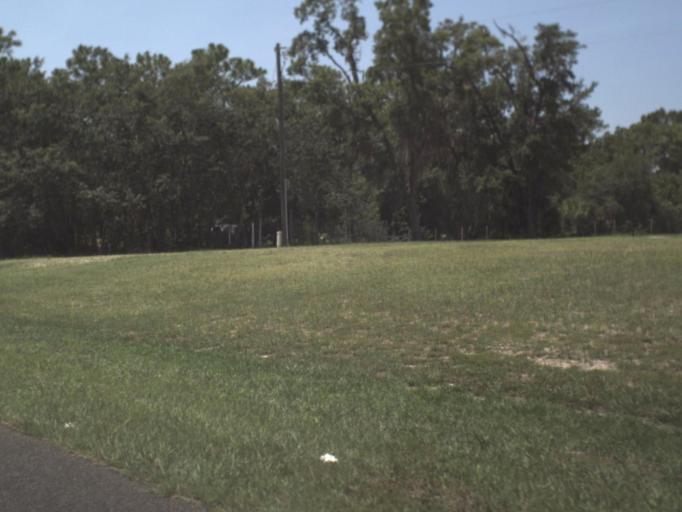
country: US
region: Florida
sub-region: Citrus County
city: Sugarmill Woods
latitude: 28.7025
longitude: -82.5527
